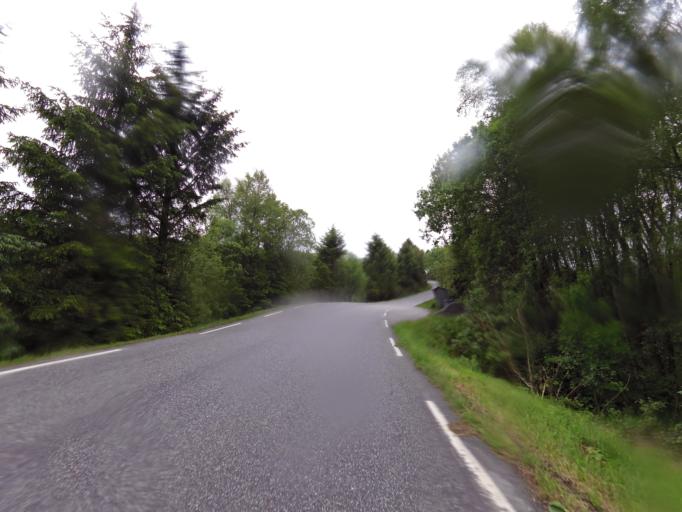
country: NO
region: Hordaland
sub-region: Sveio
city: Sveio
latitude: 59.5191
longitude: 5.2847
